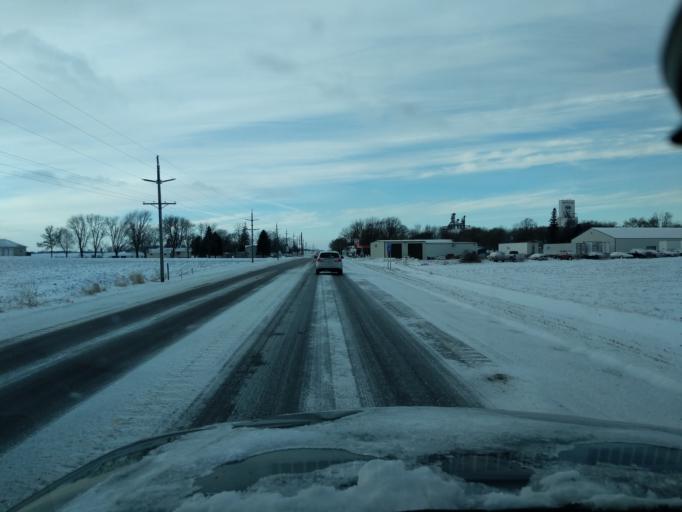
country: US
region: Minnesota
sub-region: Renville County
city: Hector
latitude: 44.7321
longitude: -94.6140
